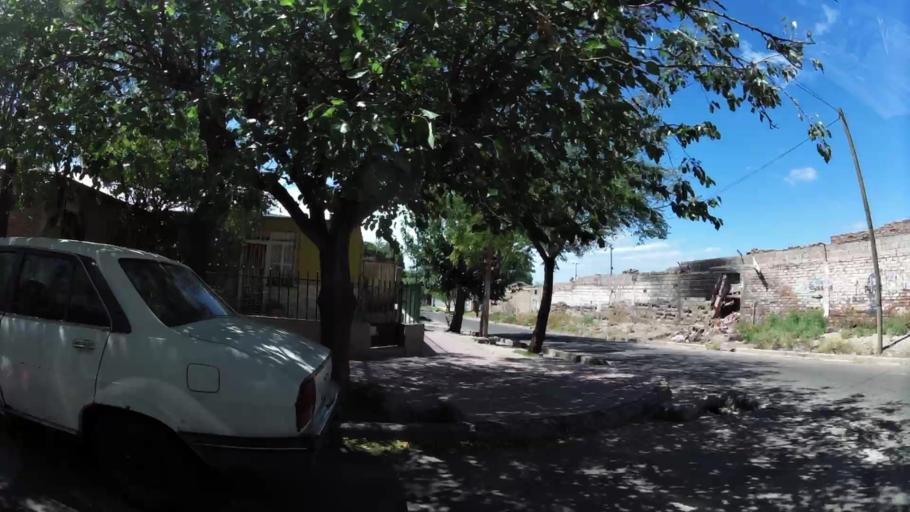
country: AR
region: Mendoza
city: Las Heras
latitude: -32.8601
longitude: -68.8604
